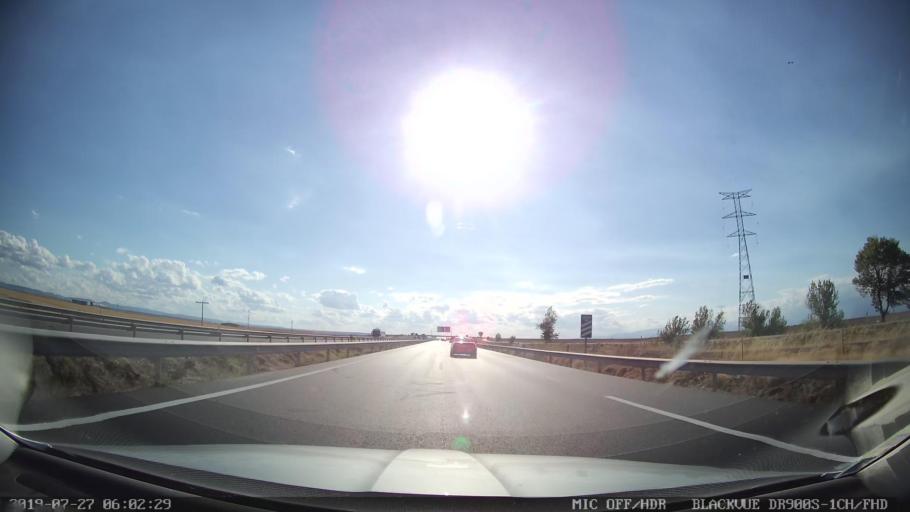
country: ES
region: Extremadura
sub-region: Provincia de Caceres
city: Berrocalejo
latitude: 39.8952
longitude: -5.3370
